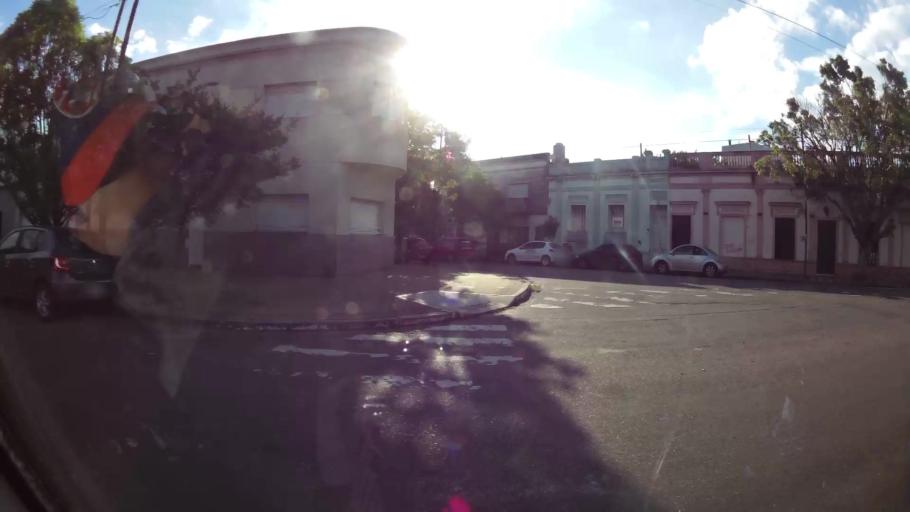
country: AR
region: Buenos Aires
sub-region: Partido de La Plata
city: La Plata
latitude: -34.9040
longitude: -57.9557
